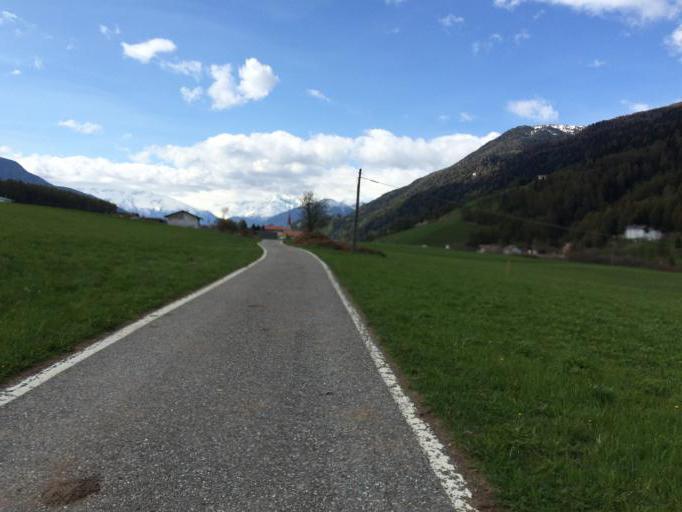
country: IT
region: Trentino-Alto Adige
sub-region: Bolzano
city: Curon Venosta
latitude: 46.7728
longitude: 10.5323
